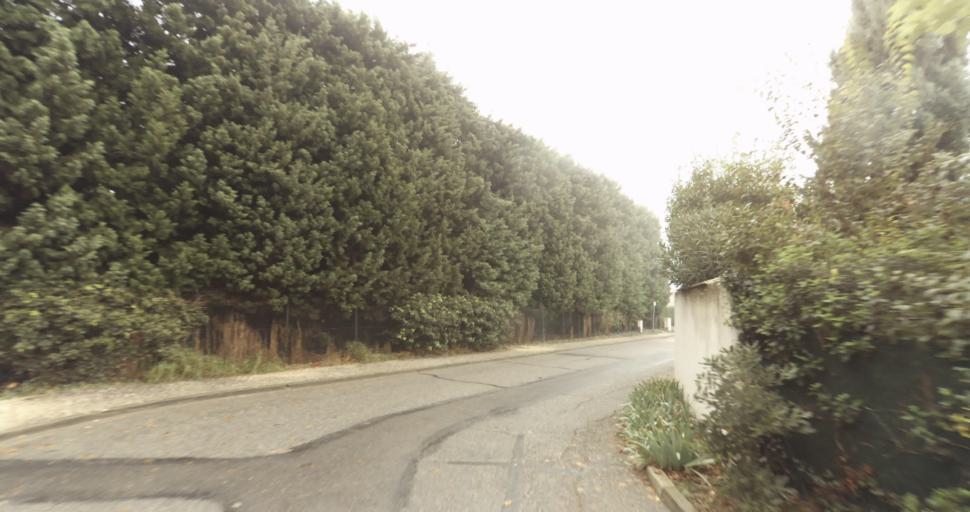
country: FR
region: Provence-Alpes-Cote d'Azur
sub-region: Departement des Bouches-du-Rhone
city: Rognonas
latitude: 43.9008
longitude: 4.8083
